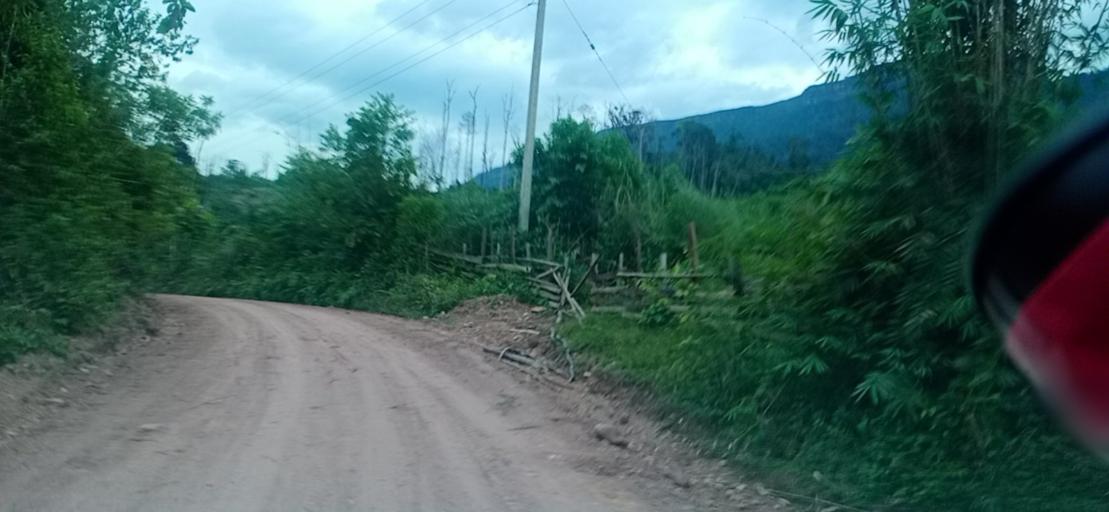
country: TH
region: Changwat Bueng Kan
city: Pak Khat
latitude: 18.5511
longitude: 103.4239
